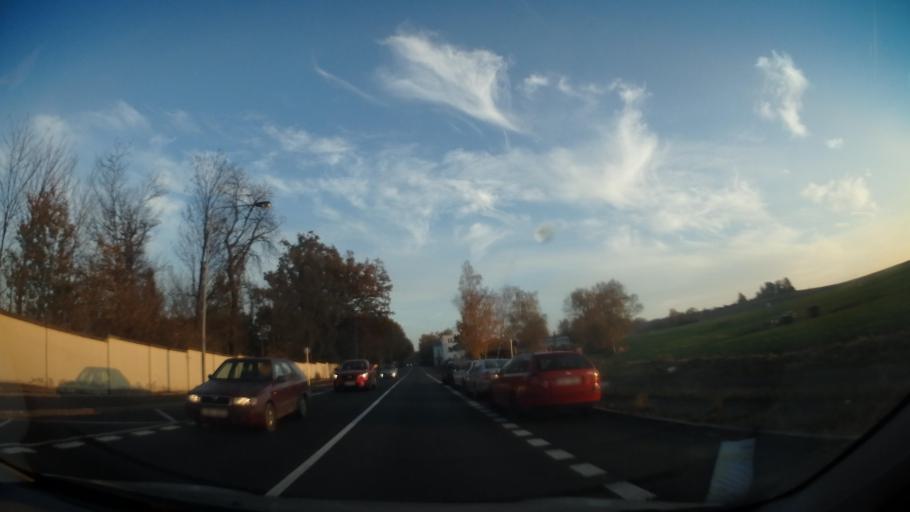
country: CZ
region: Central Bohemia
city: Vlasim
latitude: 49.6941
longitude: 14.9094
